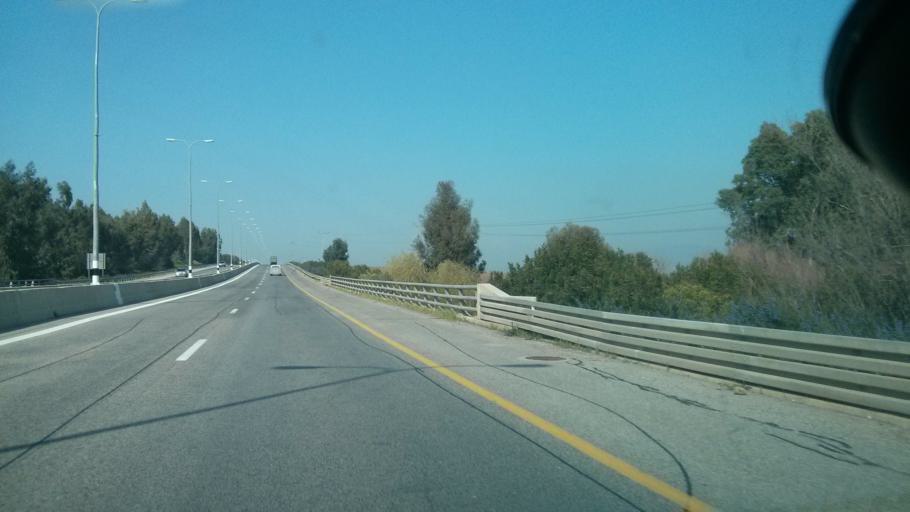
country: IL
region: Northern District
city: Rosh Pinna
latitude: 33.0835
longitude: 35.5750
